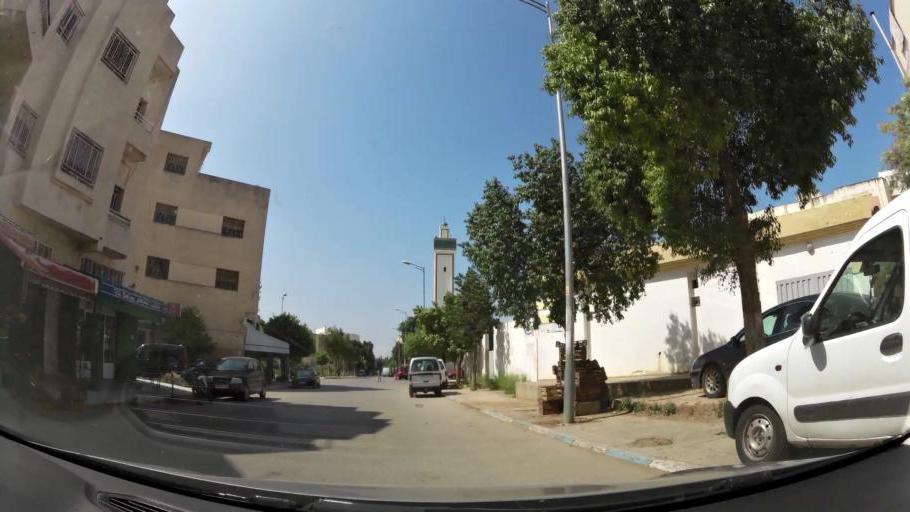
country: MA
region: Fes-Boulemane
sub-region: Fes
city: Fes
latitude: 34.0552
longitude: -5.0325
